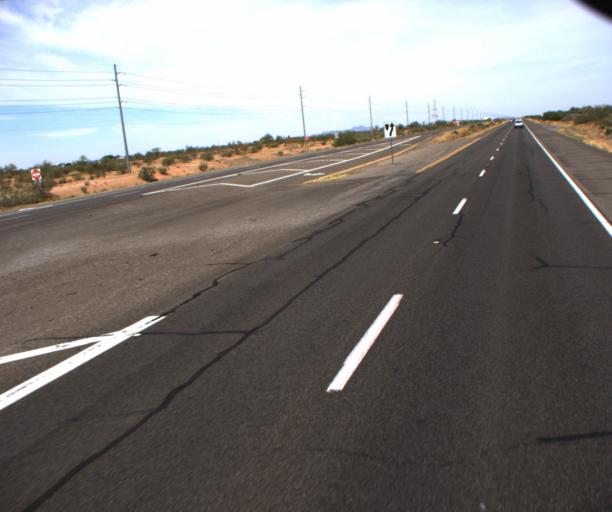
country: US
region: Arizona
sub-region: Maricopa County
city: Sun City West
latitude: 33.7264
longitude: -112.4623
